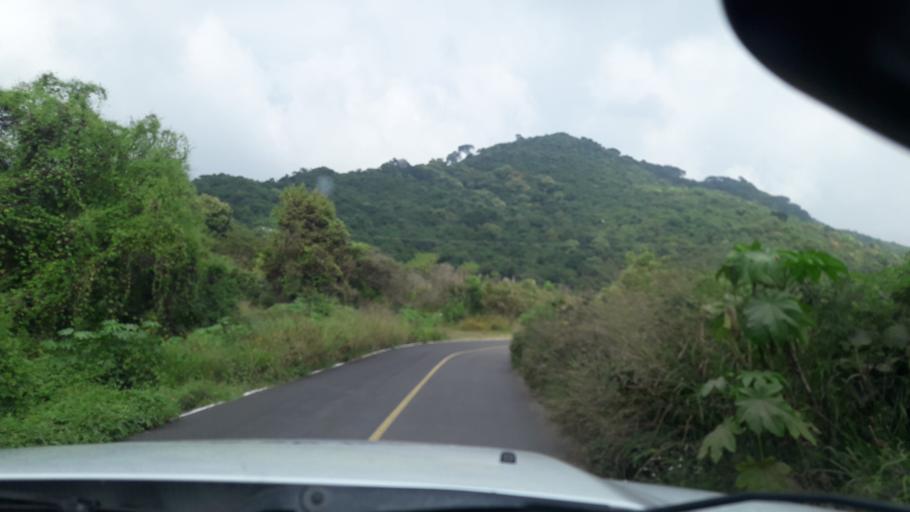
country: MX
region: Colima
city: Suchitlan
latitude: 19.4138
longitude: -103.6498
